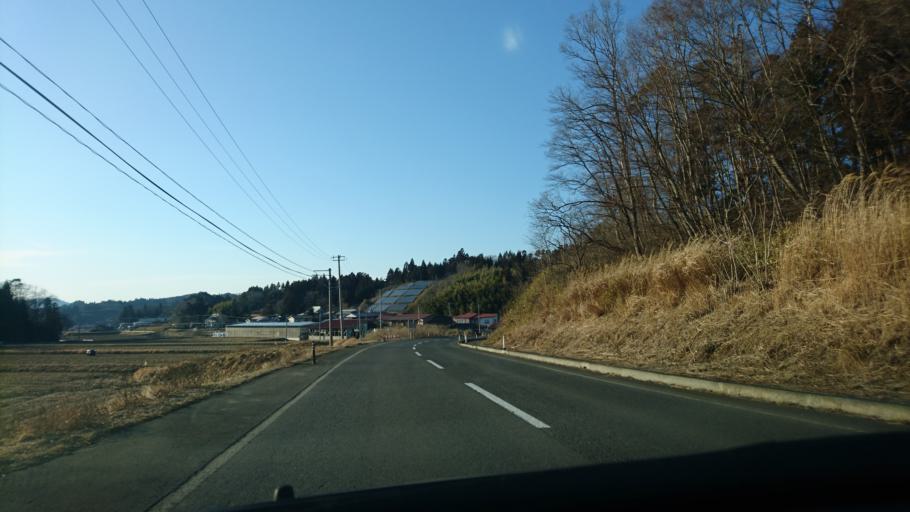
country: JP
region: Iwate
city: Ichinoseki
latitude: 38.8996
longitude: 141.3901
